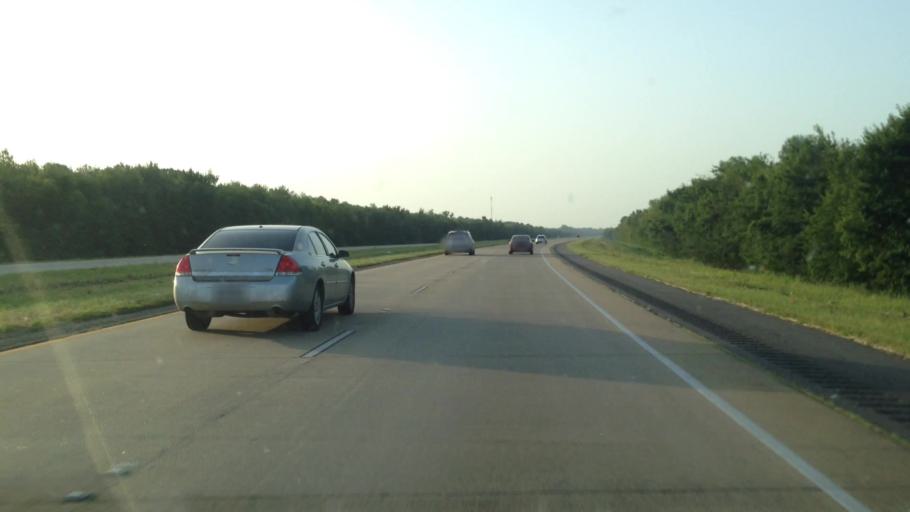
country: US
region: Louisiana
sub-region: Natchitoches Parish
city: Vienna Bend
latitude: 31.5645
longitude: -92.9875
